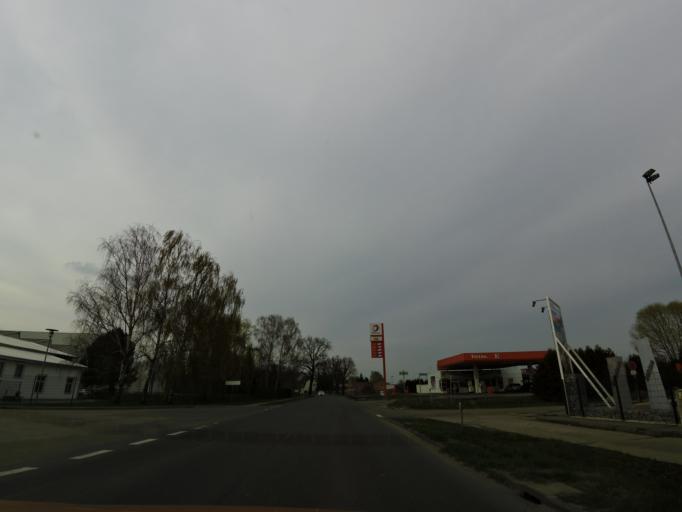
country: DE
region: Brandenburg
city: Mittenwalde
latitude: 52.2707
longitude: 13.5369
